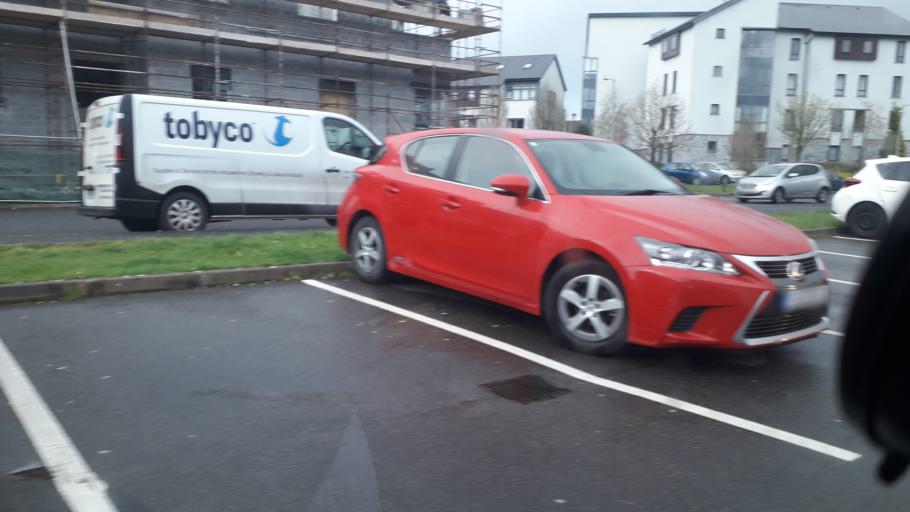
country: IE
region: Connaught
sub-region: County Leitrim
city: Carrick-on-Shannon
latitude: 53.9442
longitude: -8.0929
